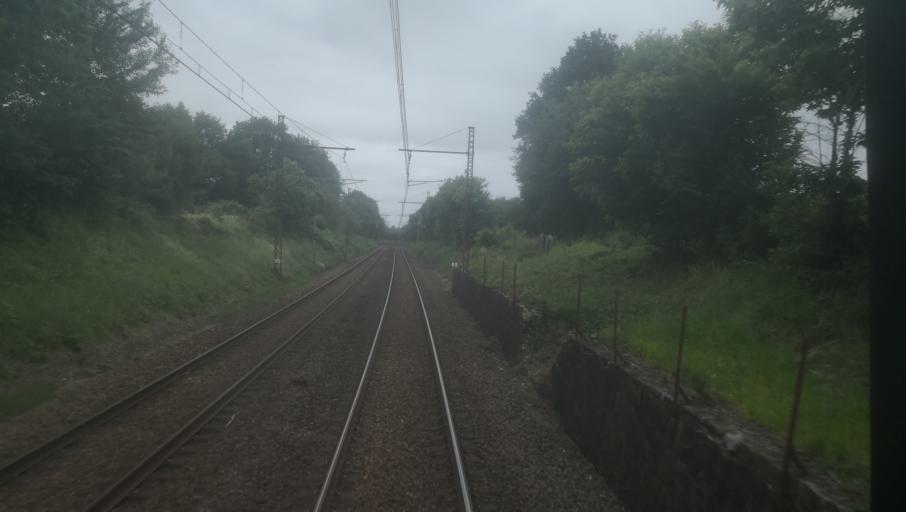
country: FR
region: Centre
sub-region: Departement de l'Indre
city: Chantome
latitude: 46.4478
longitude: 1.5519
